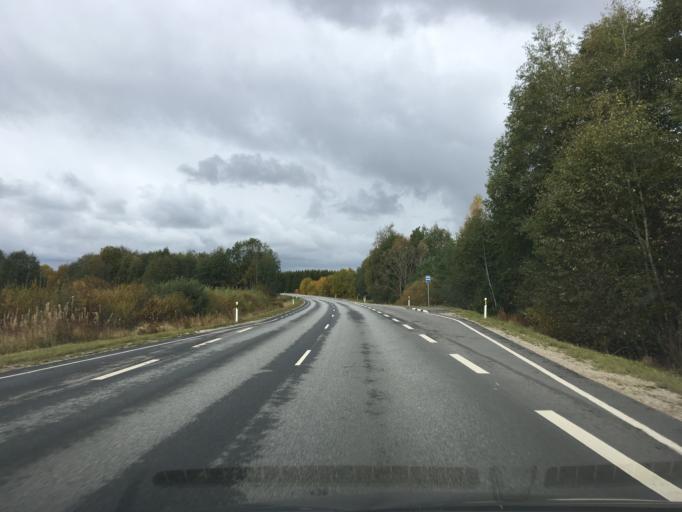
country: EE
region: Harju
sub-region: Anija vald
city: Kehra
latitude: 59.3056
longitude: 25.3569
